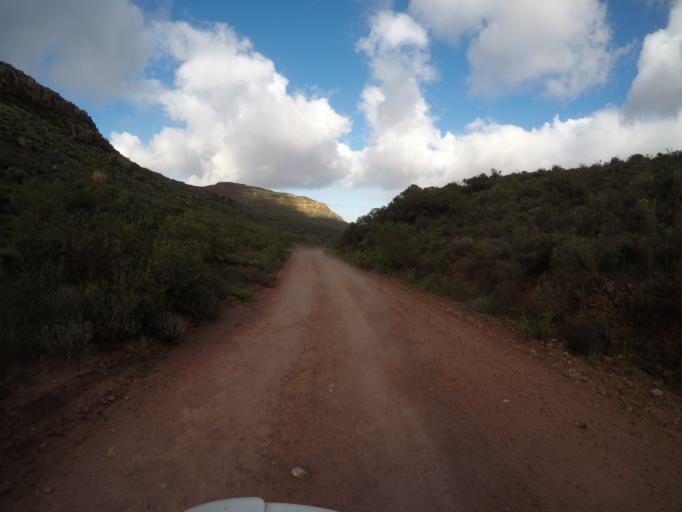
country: ZA
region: Western Cape
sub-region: West Coast District Municipality
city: Clanwilliam
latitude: -32.3406
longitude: 18.7791
